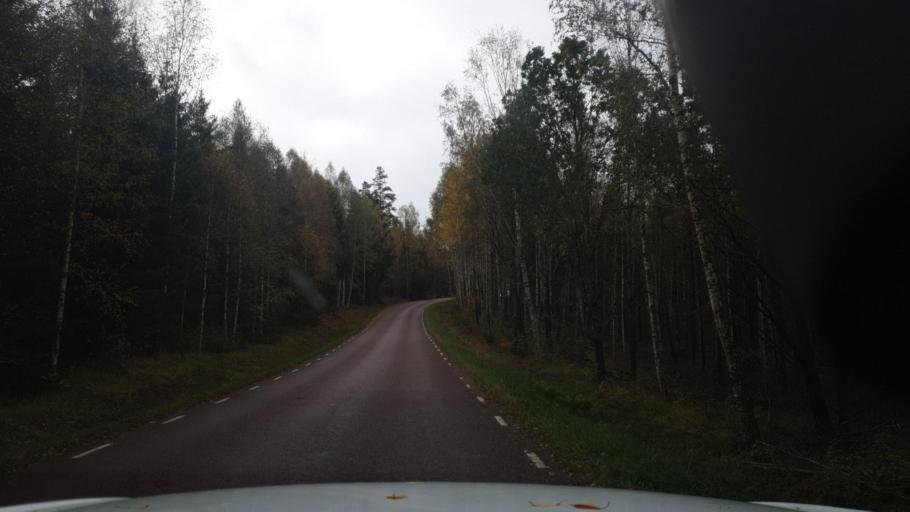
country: SE
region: Vaermland
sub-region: Grums Kommun
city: Grums
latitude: 59.4269
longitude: 13.0864
